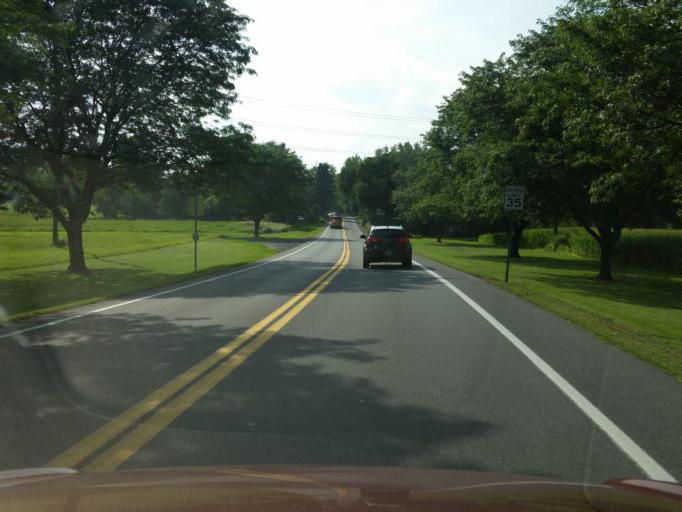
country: US
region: Pennsylvania
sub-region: Dauphin County
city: Hershey
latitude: 40.2550
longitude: -76.6303
